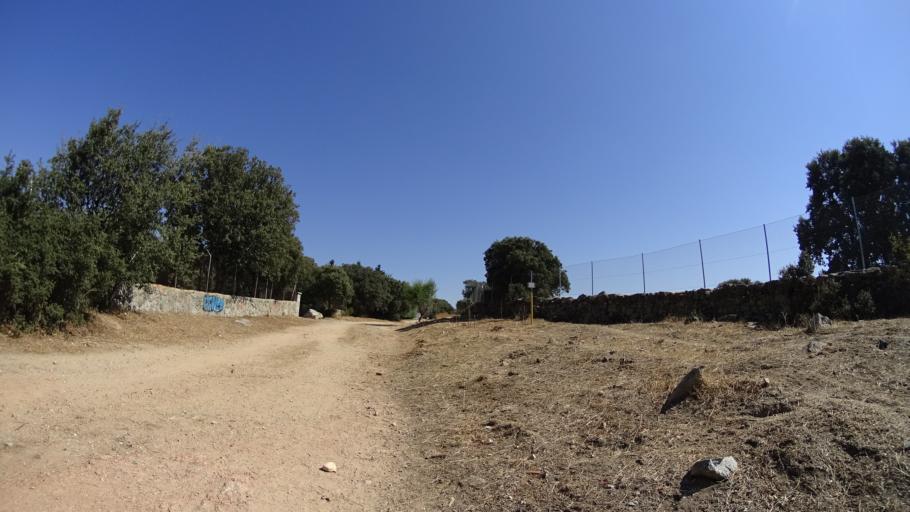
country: ES
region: Madrid
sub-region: Provincia de Madrid
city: Collado-Villalba
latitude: 40.6132
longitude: -4.0155
